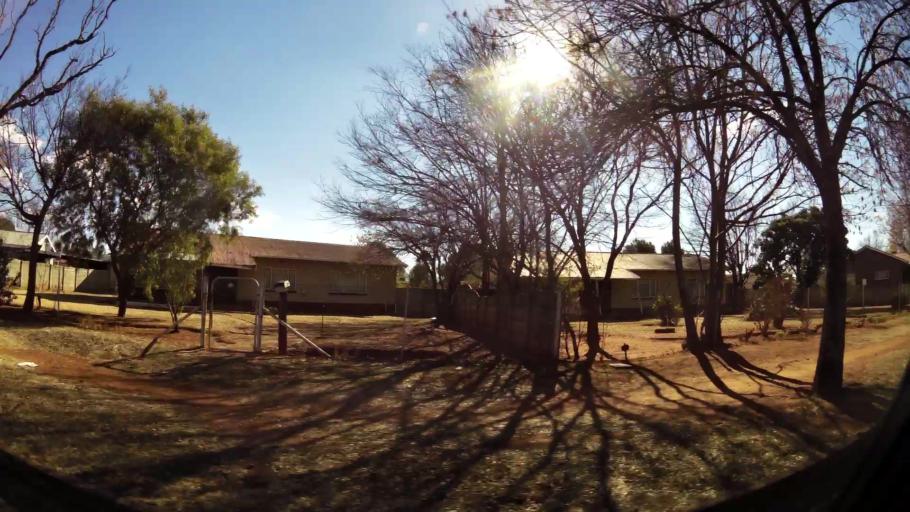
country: ZA
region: Gauteng
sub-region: West Rand District Municipality
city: Carletonville
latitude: -26.3637
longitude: 27.3797
